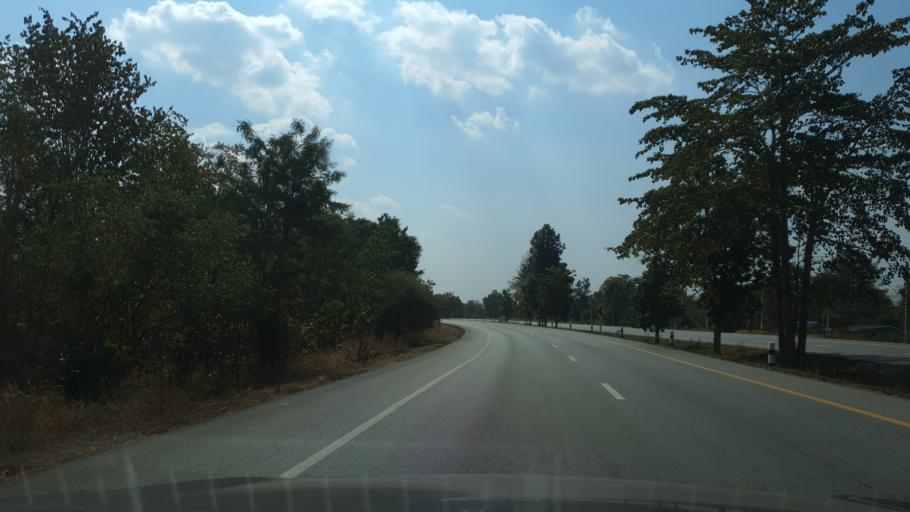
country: TH
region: Tak
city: Sam Ngao
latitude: 17.2965
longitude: 99.1436
